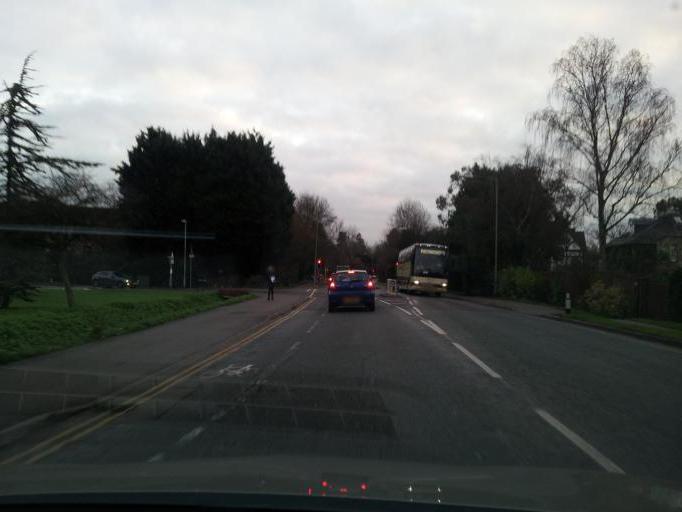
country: GB
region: England
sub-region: Cambridgeshire
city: Cambridge
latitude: 52.2114
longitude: 0.1028
